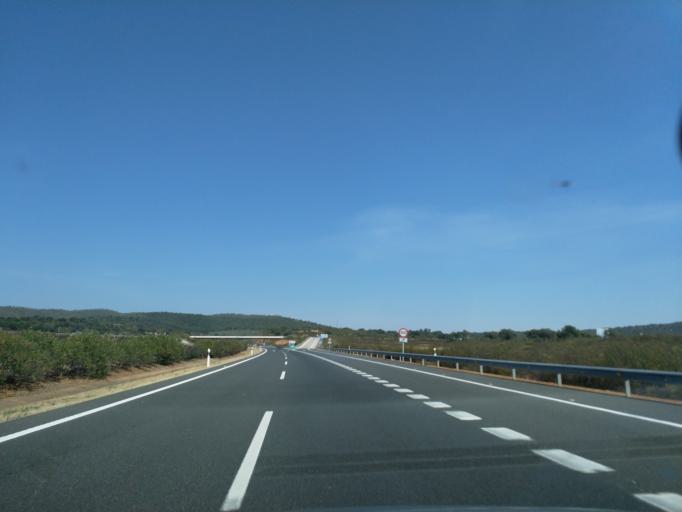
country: ES
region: Extremadura
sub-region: Provincia de Caceres
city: Alcuescar
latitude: 39.1409
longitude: -6.2730
